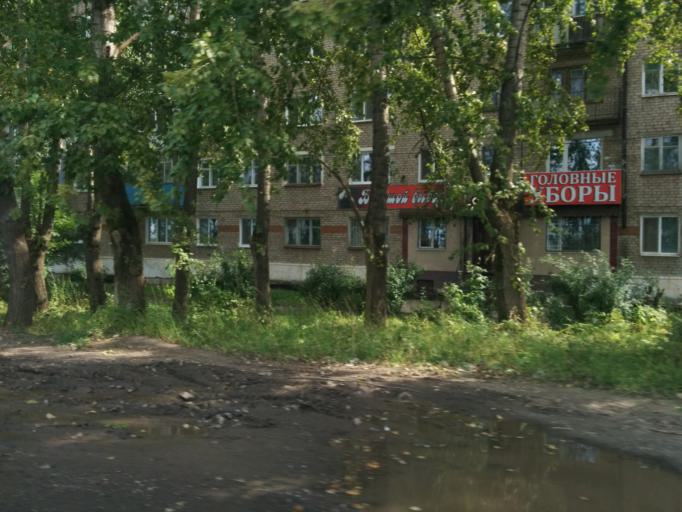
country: RU
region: Perm
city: Kudymkar
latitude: 59.0192
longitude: 54.6628
